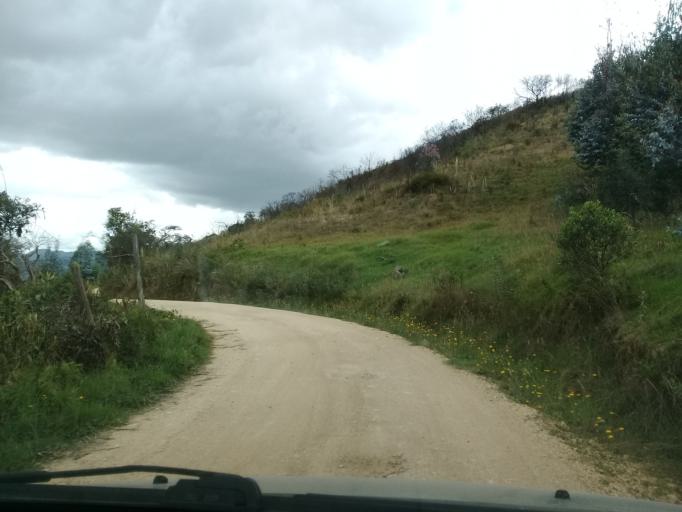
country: CO
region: Cundinamarca
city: Cucunuba
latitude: 5.2830
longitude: -73.7458
